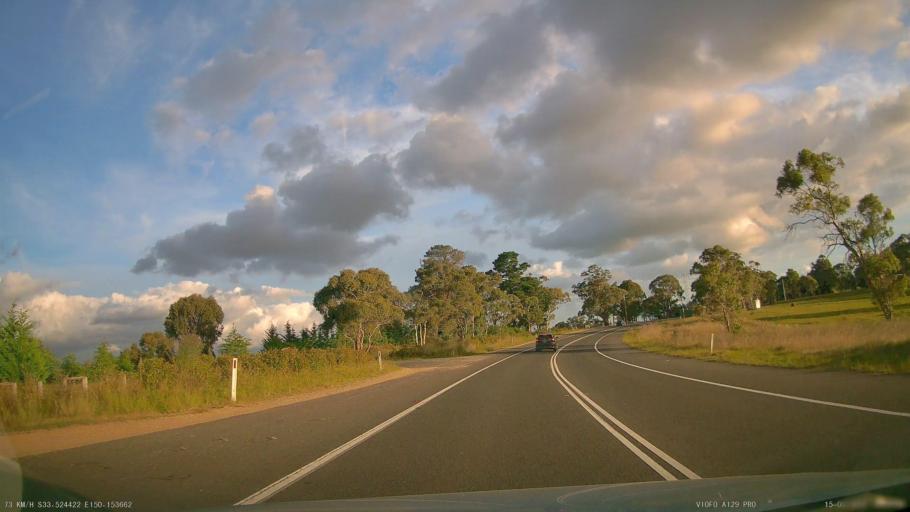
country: AU
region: New South Wales
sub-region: Lithgow
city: Bowenfels
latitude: -33.5248
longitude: 150.1537
